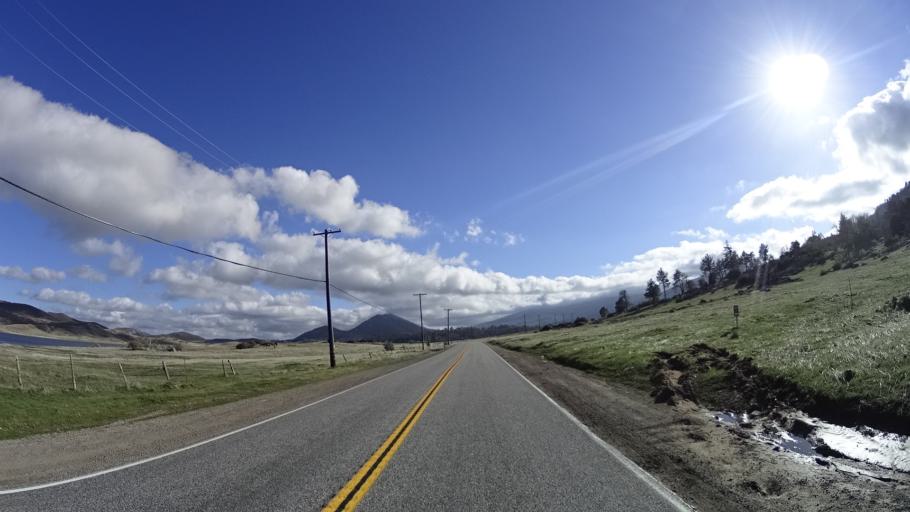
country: US
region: California
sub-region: San Diego County
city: Julian
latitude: 33.0009
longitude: -116.5661
